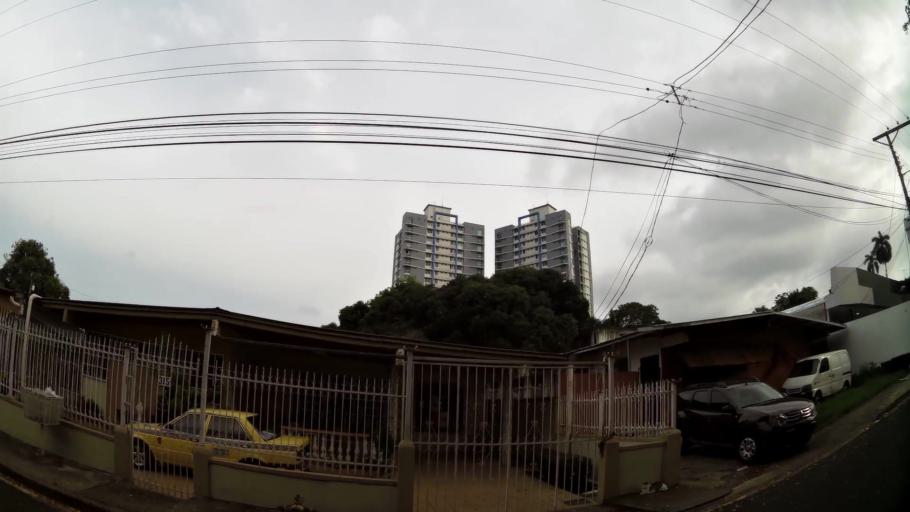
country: PA
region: Panama
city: Panama
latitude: 9.0013
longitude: -79.5114
